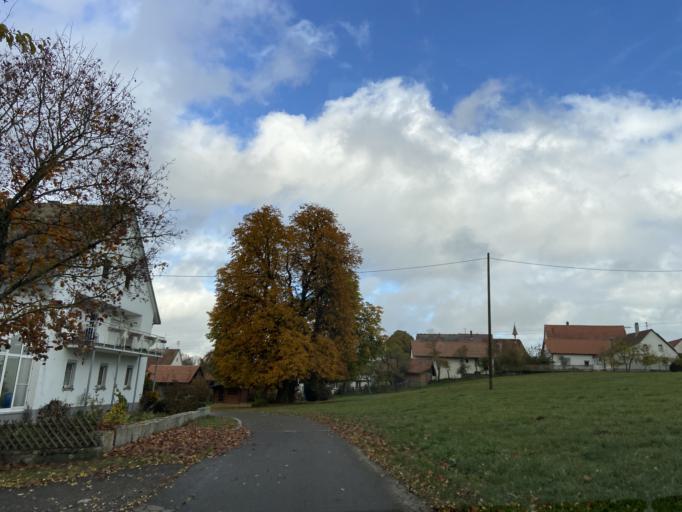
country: DE
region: Baden-Wuerttemberg
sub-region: Tuebingen Region
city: Leibertingen
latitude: 48.0570
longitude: 9.0286
